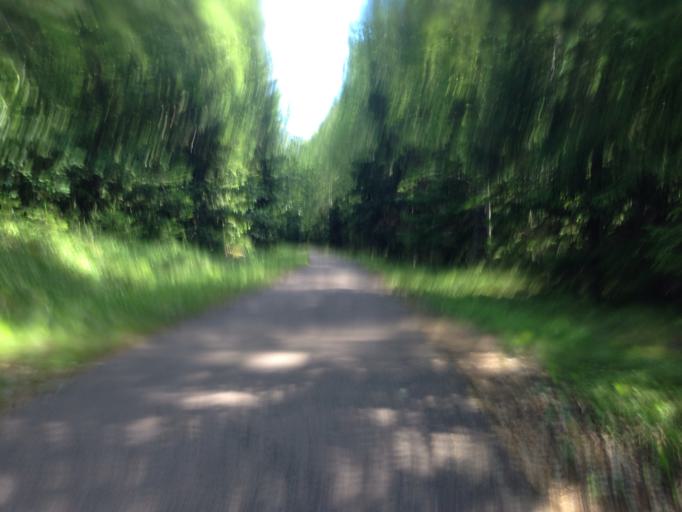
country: SE
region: Dalarna
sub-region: Ludvika Kommun
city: Grangesberg
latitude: 60.2110
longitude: 15.0493
